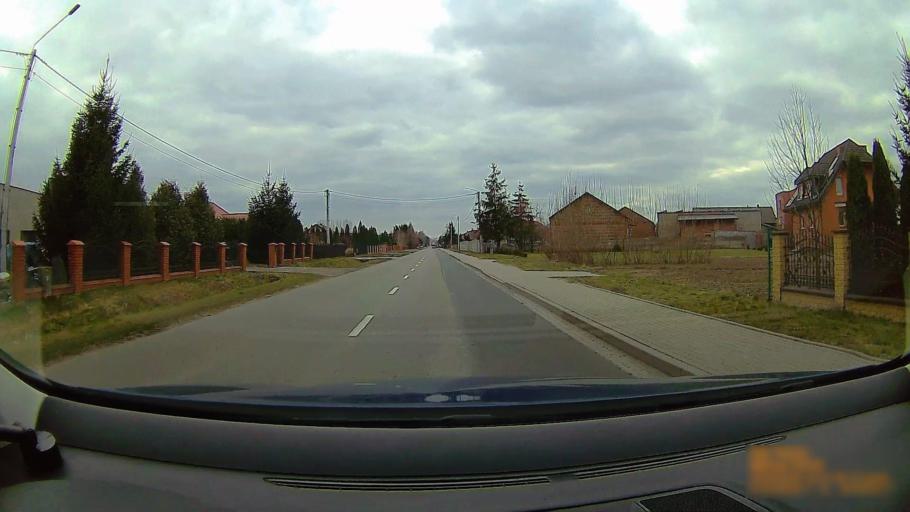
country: PL
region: Greater Poland Voivodeship
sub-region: Powiat koninski
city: Rzgow Pierwszy
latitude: 52.1584
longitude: 18.0586
